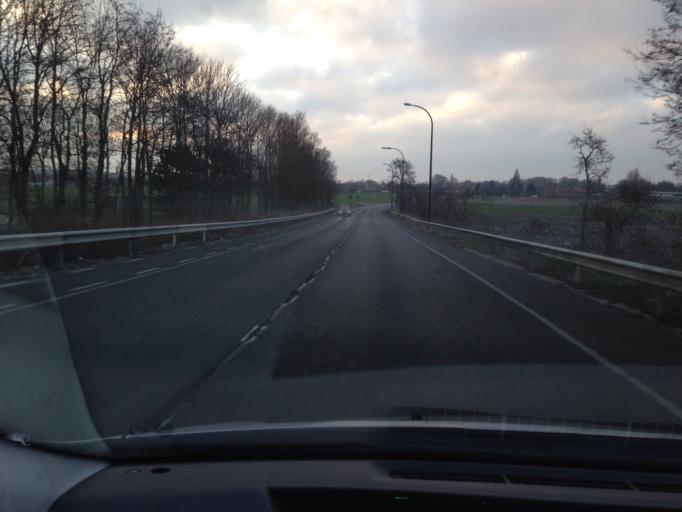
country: BE
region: Flanders
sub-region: Provincie West-Vlaanderen
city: Gistel
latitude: 51.1670
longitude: 2.9668
